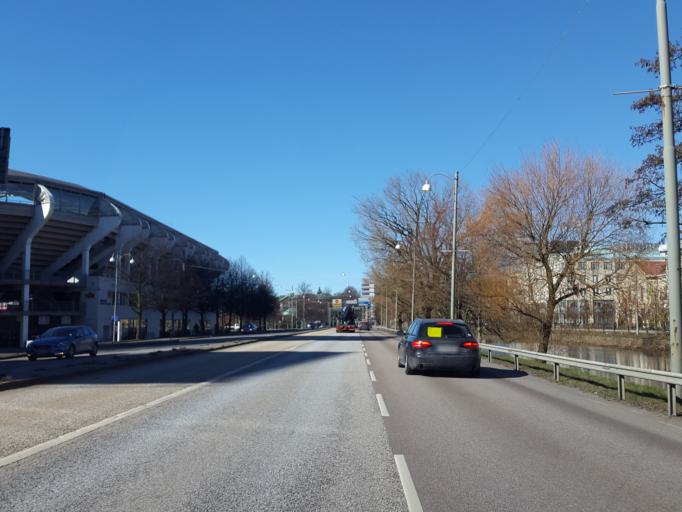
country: SE
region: Vaestra Goetaland
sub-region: Goteborg
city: Goeteborg
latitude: 57.7076
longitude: 11.9823
